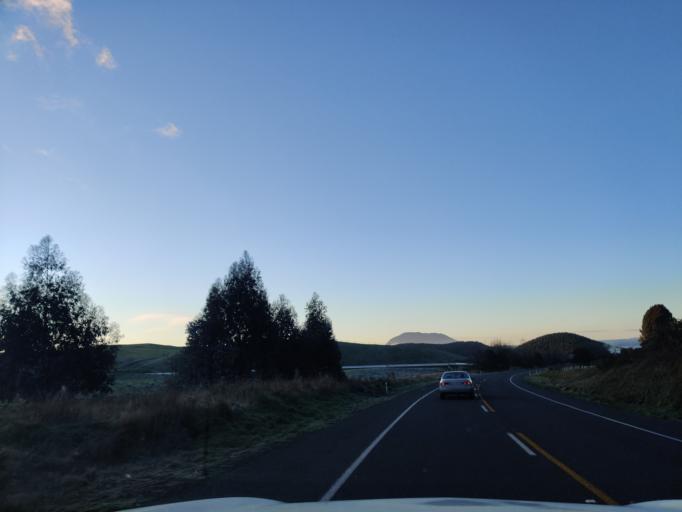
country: NZ
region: Waikato
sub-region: Taupo District
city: Taupo
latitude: -38.6287
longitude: 176.0436
